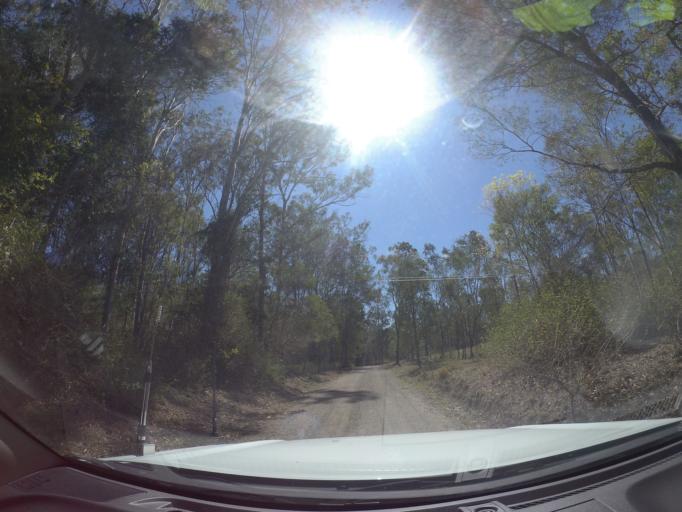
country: AU
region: Queensland
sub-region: Ipswich
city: Springfield Lakes
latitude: -27.7553
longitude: 152.8865
